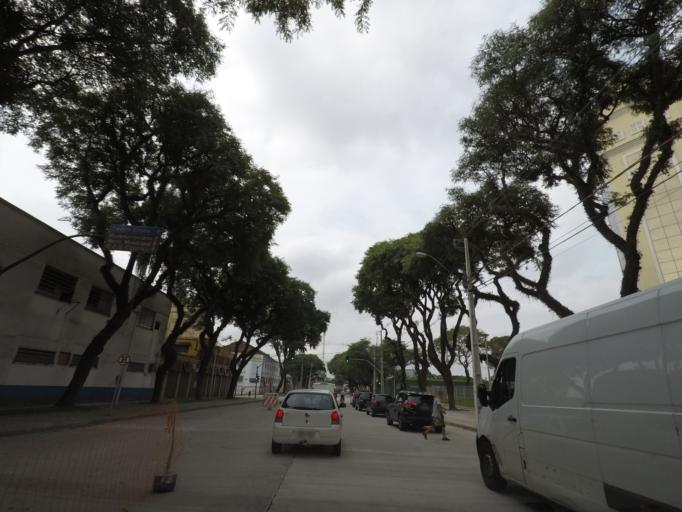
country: BR
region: Parana
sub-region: Curitiba
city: Curitiba
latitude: -25.4412
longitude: -49.2620
